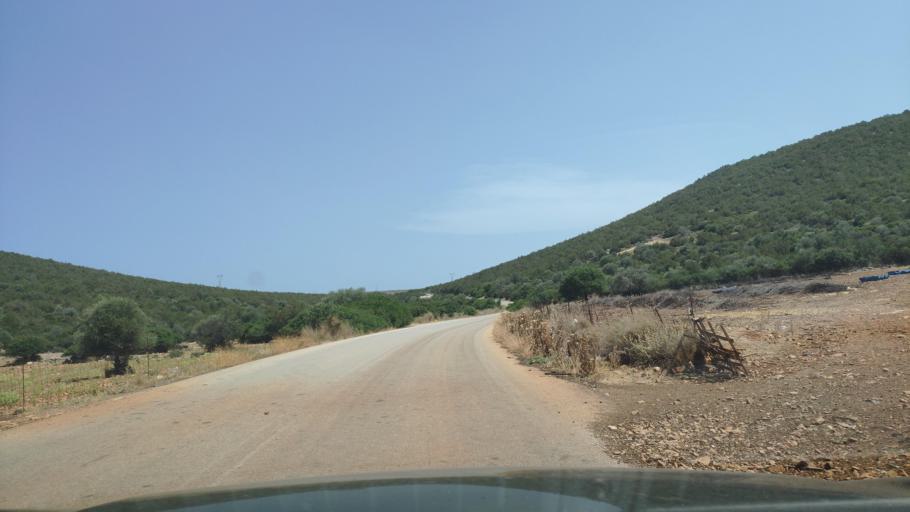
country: GR
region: Peloponnese
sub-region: Nomos Argolidos
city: Didyma
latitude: 37.4490
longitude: 23.1799
